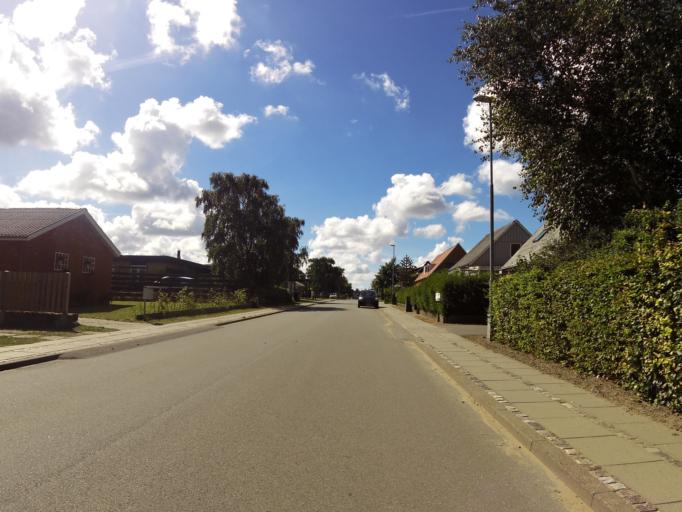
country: DK
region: South Denmark
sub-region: Esbjerg Kommune
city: Ribe
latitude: 55.3266
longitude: 8.7937
